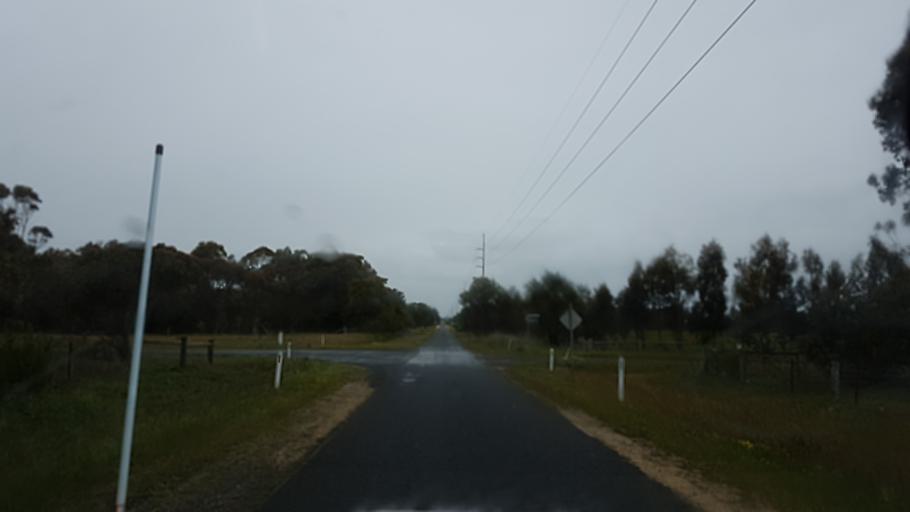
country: AU
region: Victoria
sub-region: Ballarat North
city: Mount Clear
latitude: -37.7833
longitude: 143.9803
